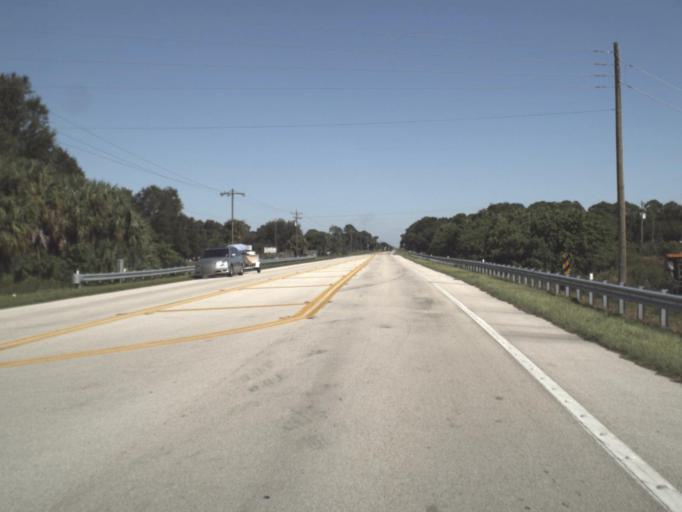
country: US
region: Florida
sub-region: Hendry County
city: Port LaBelle
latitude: 26.7683
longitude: -81.2478
